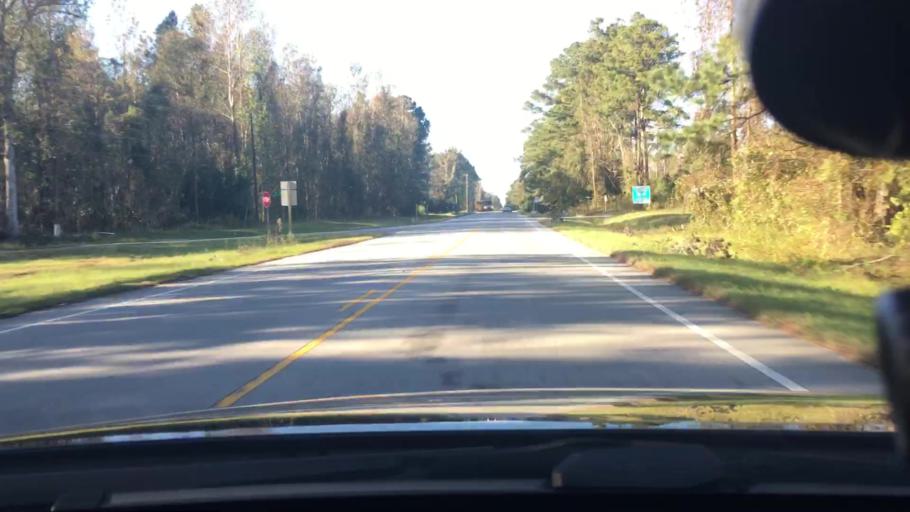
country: US
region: North Carolina
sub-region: Craven County
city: New Bern
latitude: 35.1945
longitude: -77.0539
